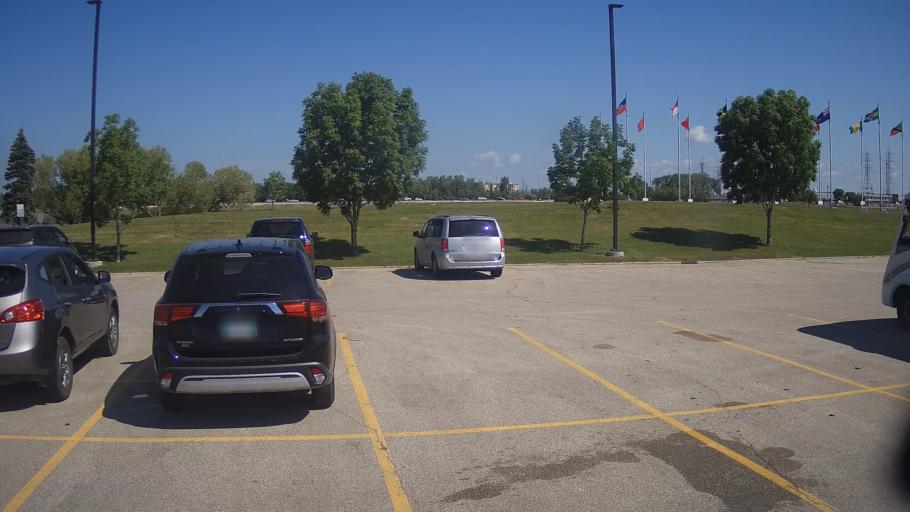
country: CA
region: Manitoba
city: Winnipeg
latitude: 49.8526
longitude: -97.0526
